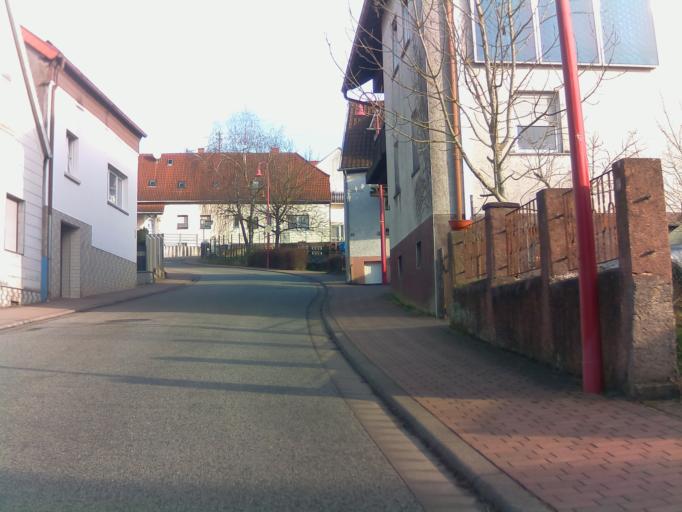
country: DE
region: Rheinland-Pfalz
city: Gries
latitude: 49.4193
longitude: 7.4008
